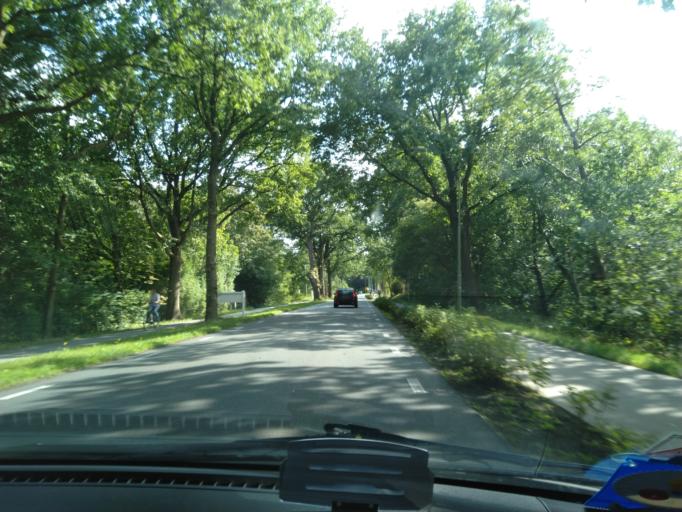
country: NL
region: Groningen
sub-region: Gemeente Groningen
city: Groningen
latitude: 53.1662
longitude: 6.5550
